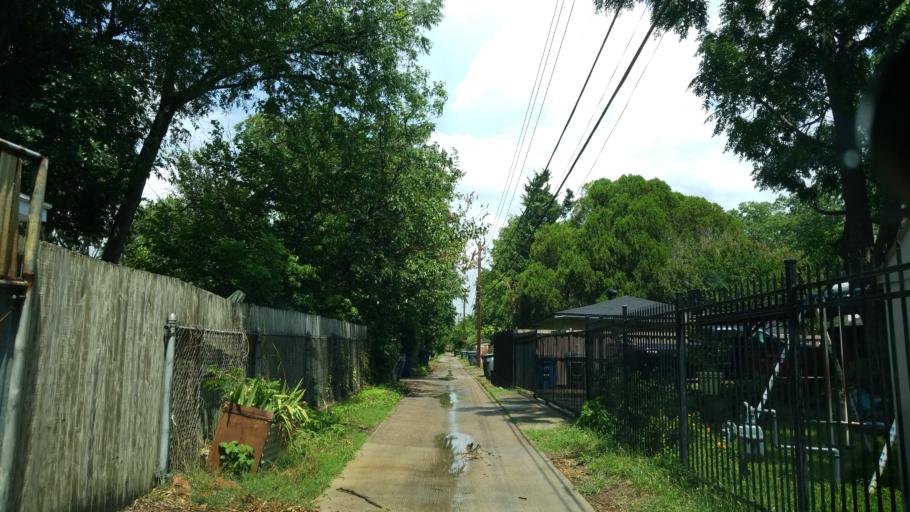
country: US
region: Texas
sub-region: Dallas County
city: Farmers Branch
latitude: 32.8804
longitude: -96.8681
